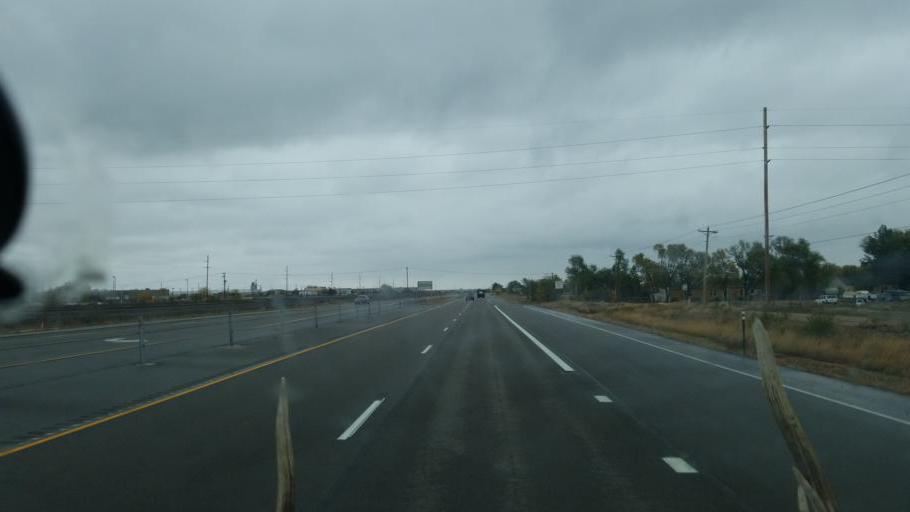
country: US
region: Colorado
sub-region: Pueblo County
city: Pueblo
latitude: 38.2752
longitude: -104.4899
